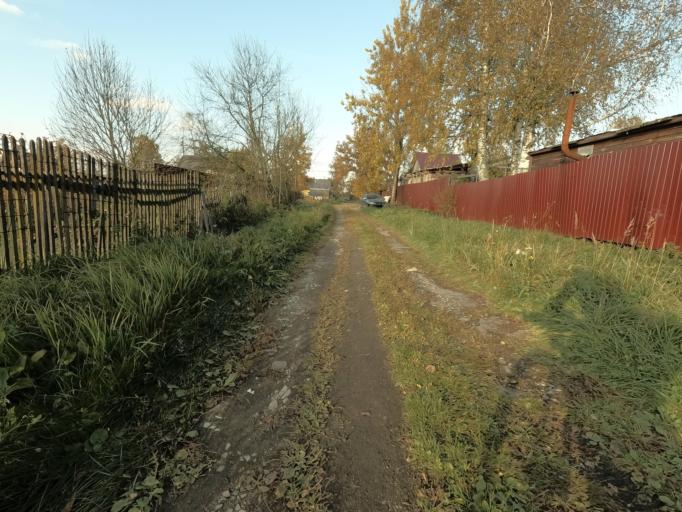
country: RU
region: Leningrad
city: Mga
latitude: 59.7489
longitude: 31.0631
